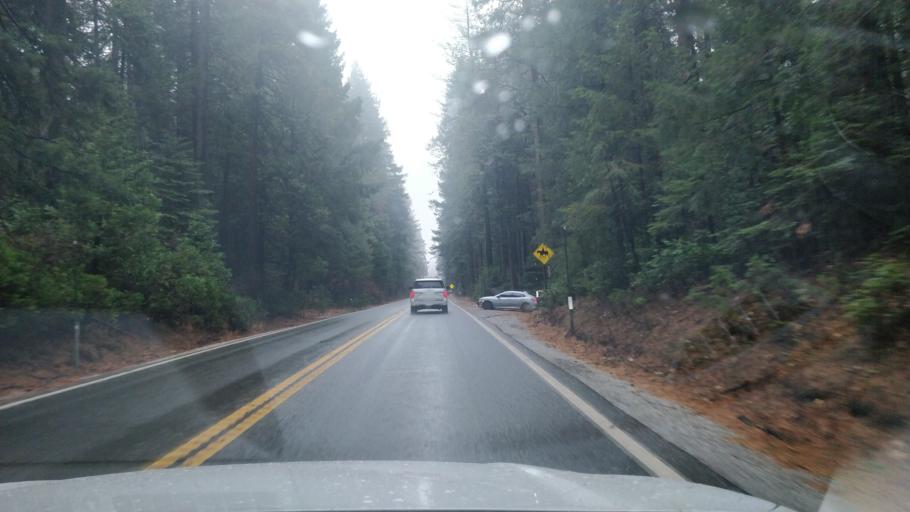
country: US
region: California
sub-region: Nevada County
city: Nevada City
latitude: 39.3225
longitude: -120.8520
